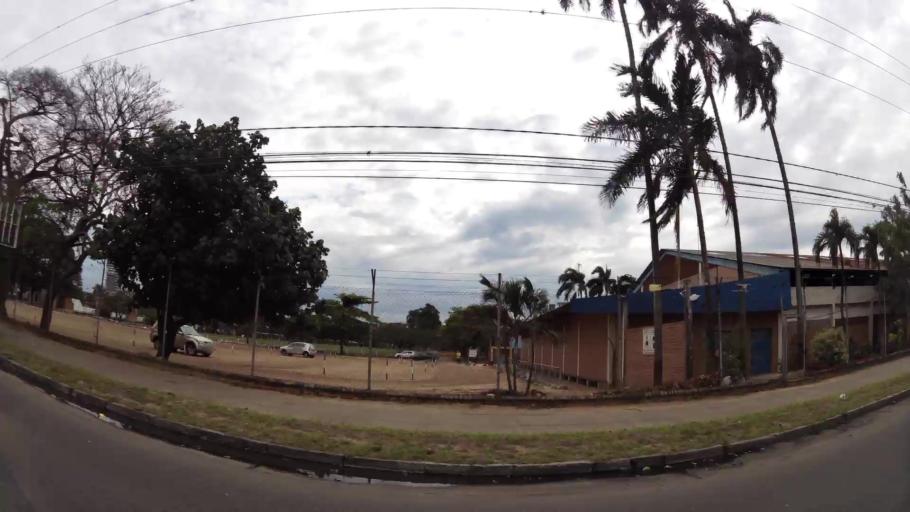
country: BO
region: Santa Cruz
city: Santa Cruz de la Sierra
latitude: -17.7715
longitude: -63.1875
